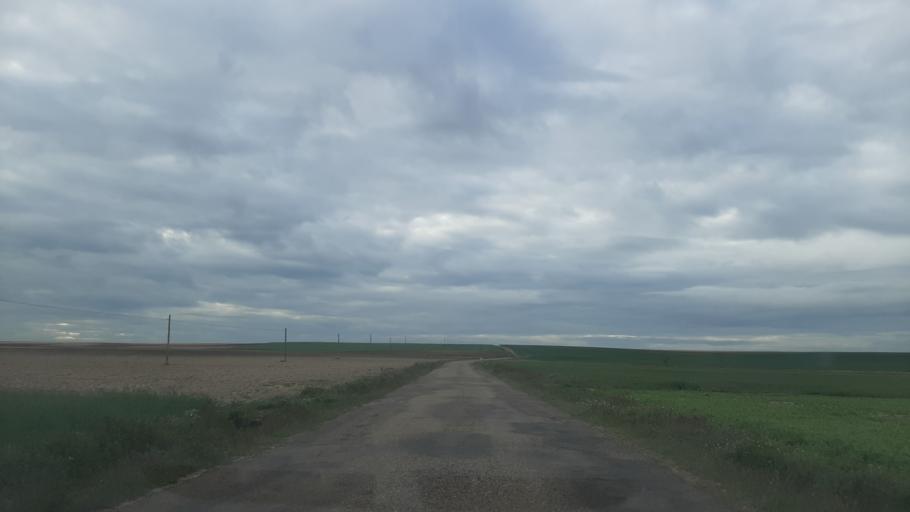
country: ES
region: Castille and Leon
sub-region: Provincia de Salamanca
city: Villaflores
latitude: 41.0738
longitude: -5.2130
